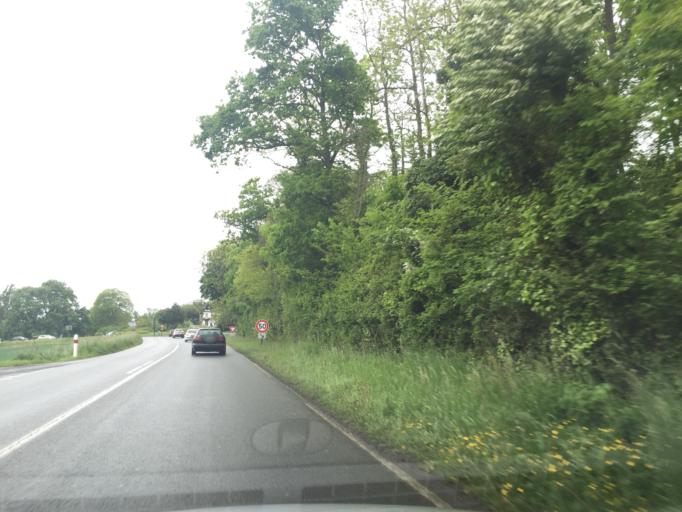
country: FR
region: Brittany
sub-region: Departement des Cotes-d'Armor
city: Ploubalay
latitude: 48.5737
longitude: -2.1767
